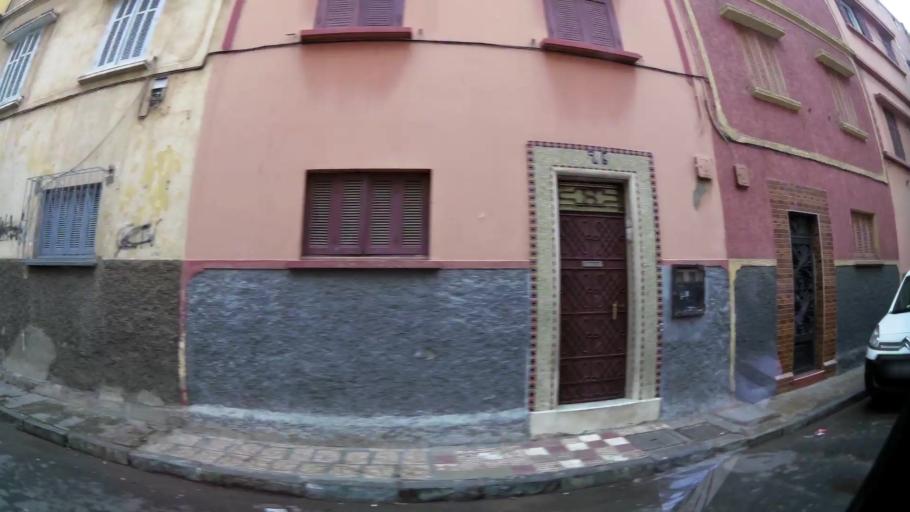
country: MA
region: Grand Casablanca
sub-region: Casablanca
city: Casablanca
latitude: 33.5479
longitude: -7.5681
